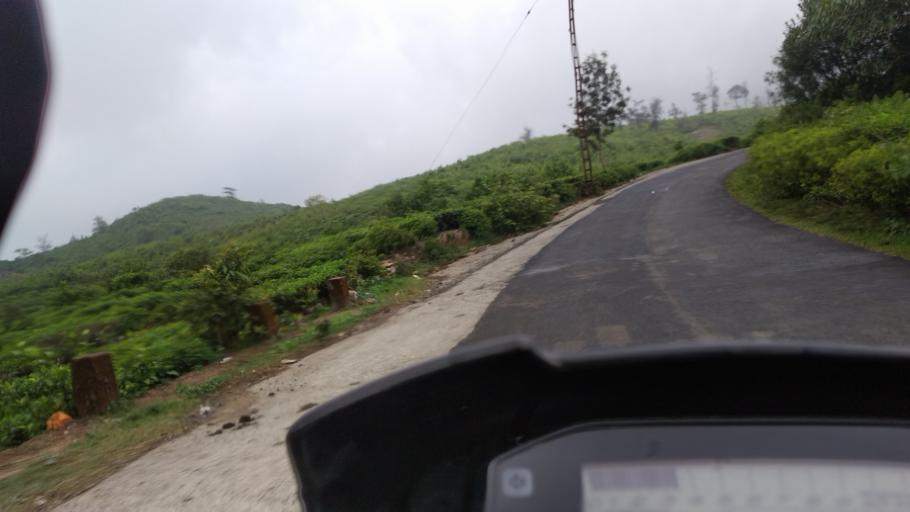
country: IN
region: Kerala
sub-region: Kottayam
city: Erattupetta
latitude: 9.6374
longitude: 76.9343
